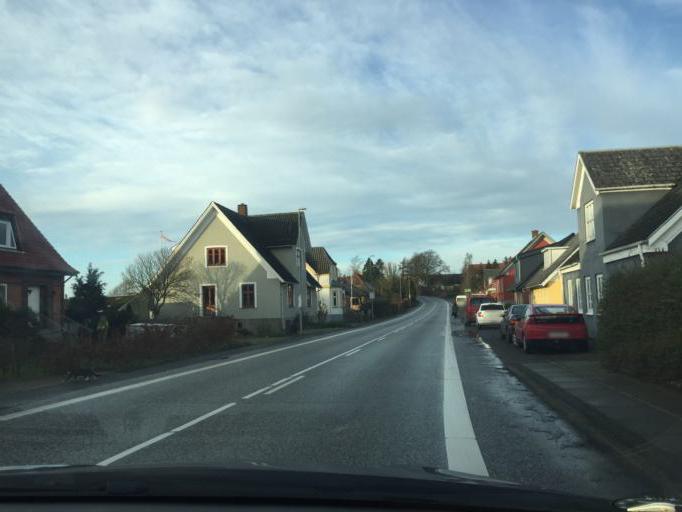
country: DK
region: South Denmark
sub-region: Faaborg-Midtfyn Kommune
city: Ringe
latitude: 55.2011
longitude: 10.4106
